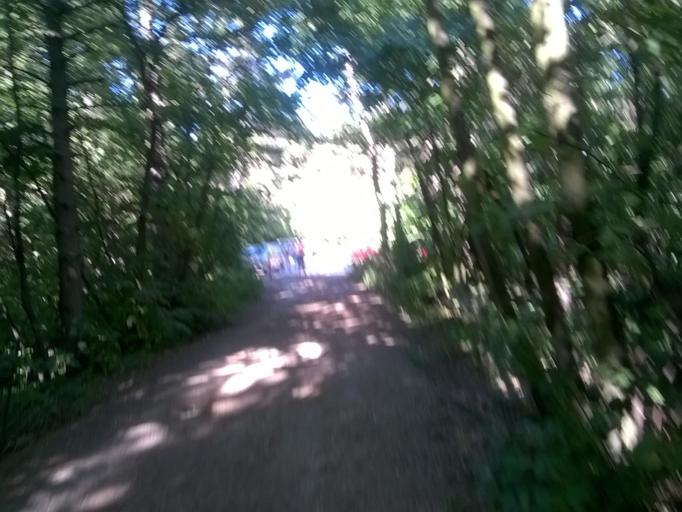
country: SK
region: Nitriansky
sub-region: Okres Nitra
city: Nitra
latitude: 48.3572
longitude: 18.0592
